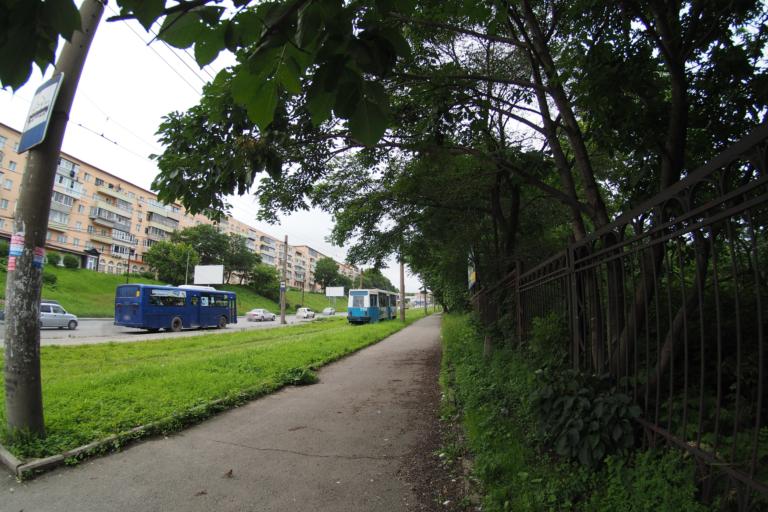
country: RU
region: Primorskiy
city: Vladivostok
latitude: 43.1213
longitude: 131.9383
